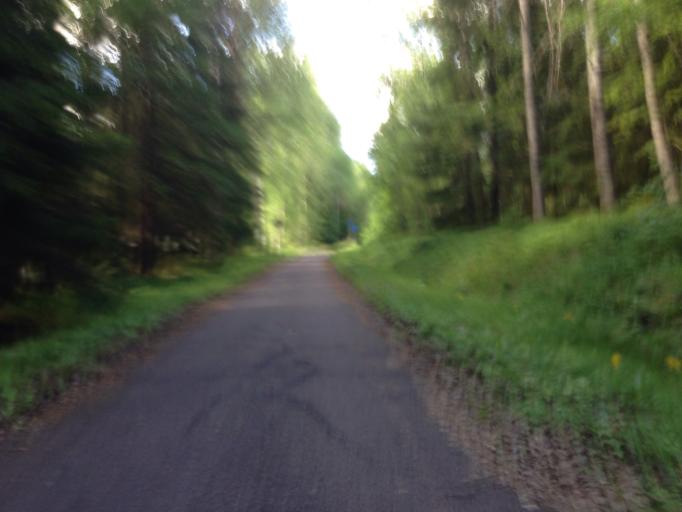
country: SE
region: Dalarna
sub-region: Ludvika Kommun
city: Grangesberg
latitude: 60.2086
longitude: 15.0528
